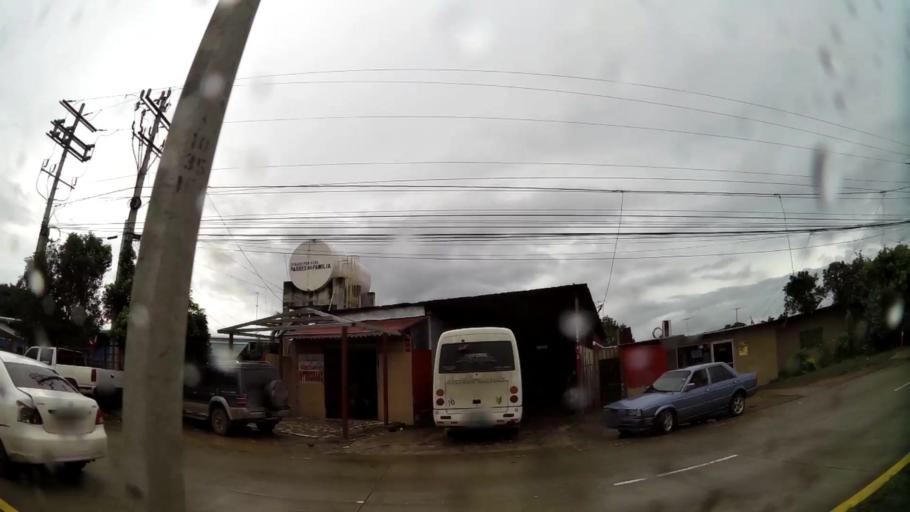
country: PA
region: Veraguas
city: Santiago de Veraguas
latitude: 8.0990
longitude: -80.9719
